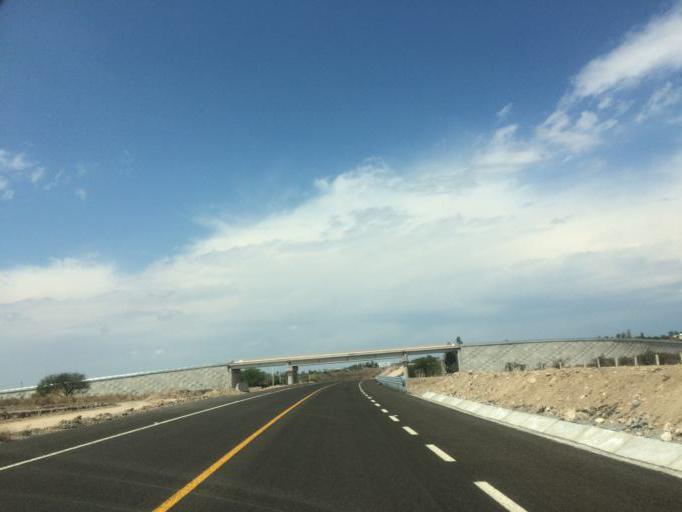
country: MX
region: Guanajuato
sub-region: Silao de la Victoria
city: El Refugio de los Sauces
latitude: 21.0333
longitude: -101.5039
